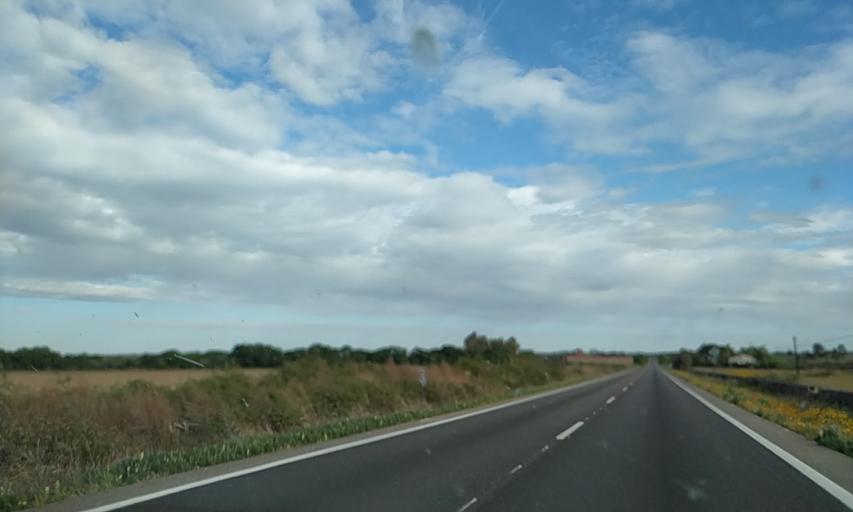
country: ES
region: Extremadura
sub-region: Provincia de Caceres
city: Huelaga
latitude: 40.0453
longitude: -6.6349
